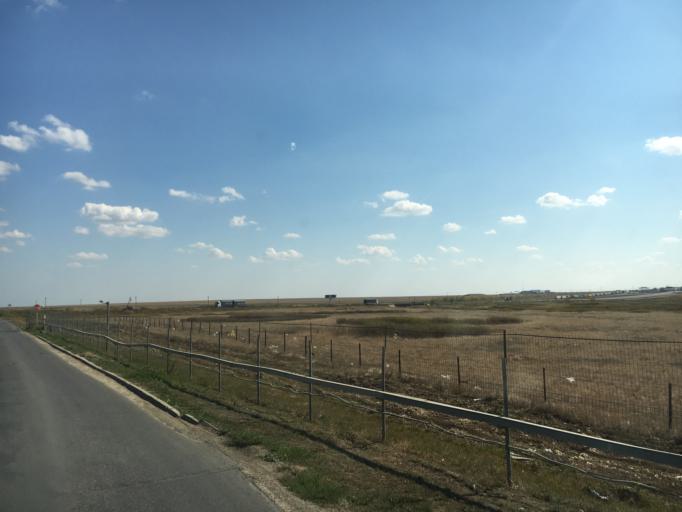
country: KZ
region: Batys Qazaqstan
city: Peremetnoe
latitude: 51.6762
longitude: 51.0001
